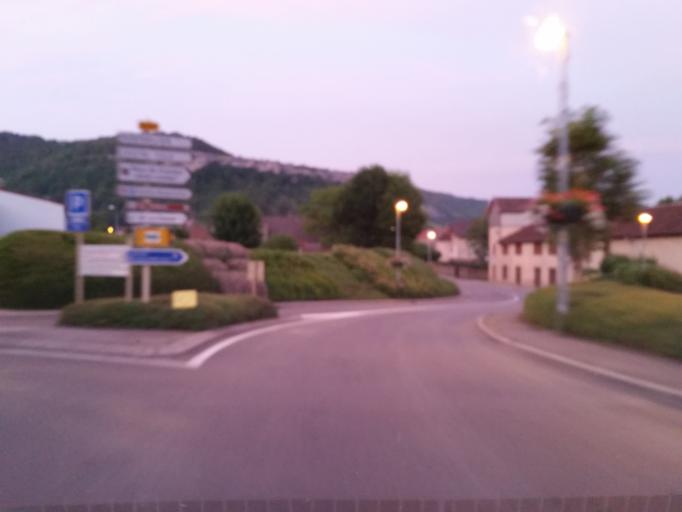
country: FR
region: Franche-Comte
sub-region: Departement du Doubs
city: Ornans
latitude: 47.1065
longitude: 6.1376
